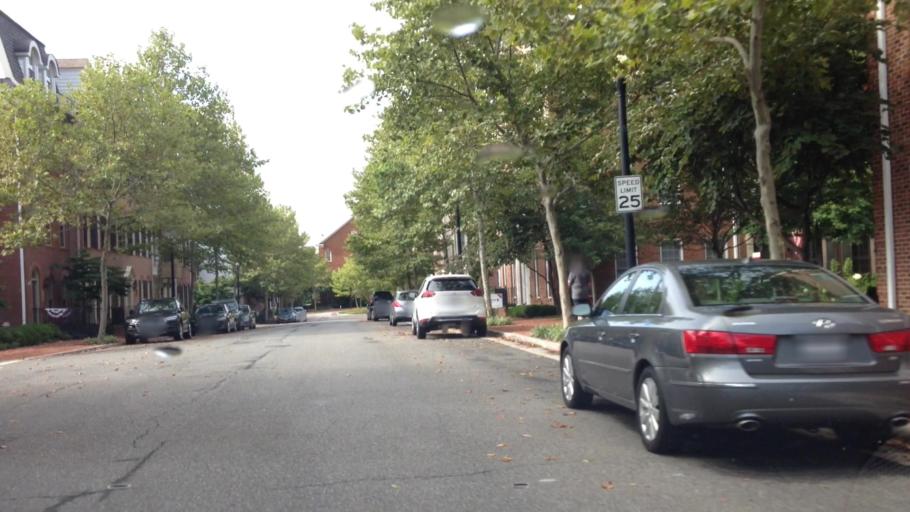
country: US
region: Virginia
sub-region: City of Alexandria
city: Alexandria
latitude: 38.8281
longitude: -77.0457
